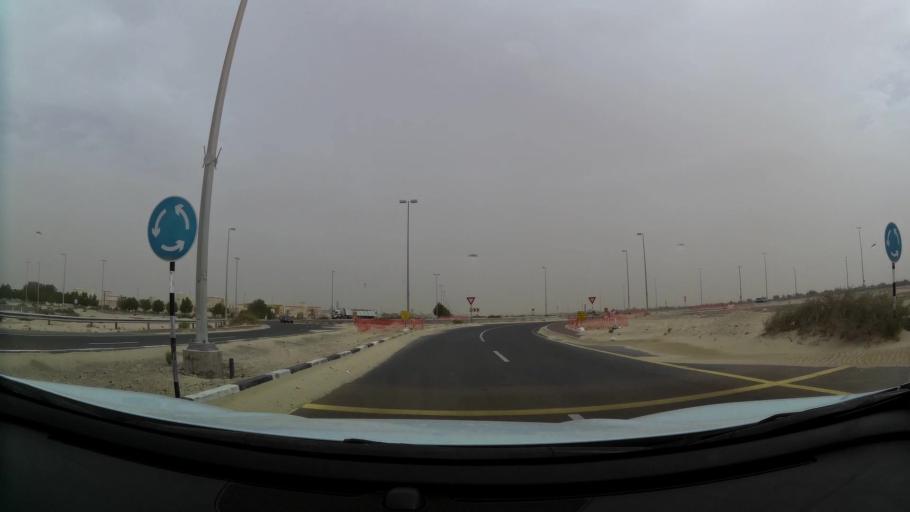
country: AE
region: Abu Dhabi
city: Abu Dhabi
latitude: 24.3603
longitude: 54.7165
